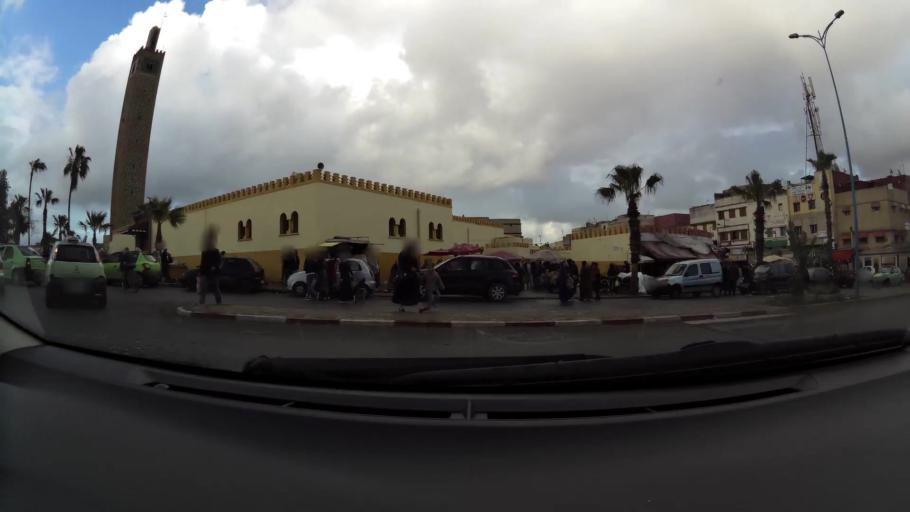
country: MA
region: Grand Casablanca
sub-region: Mohammedia
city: Mohammedia
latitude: 33.6865
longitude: -7.3899
